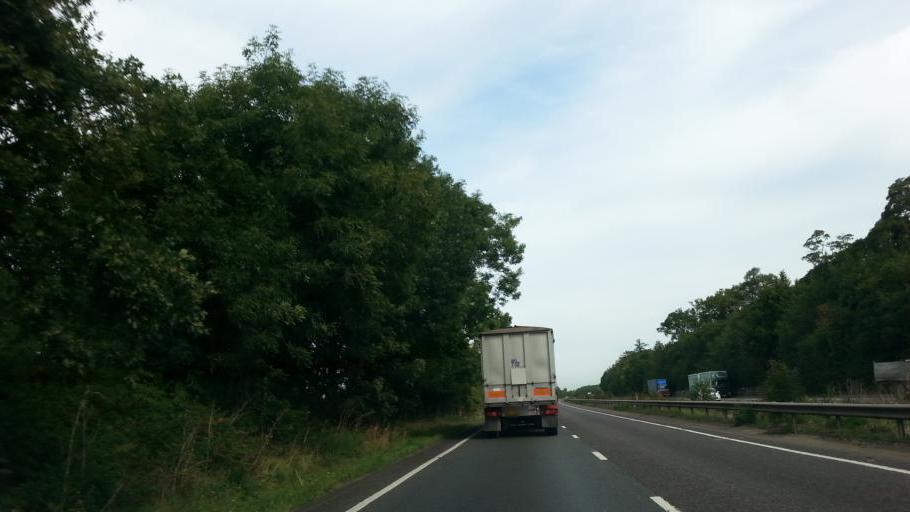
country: GB
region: England
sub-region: Suffolk
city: Needham Market
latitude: 52.1372
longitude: 1.0870
